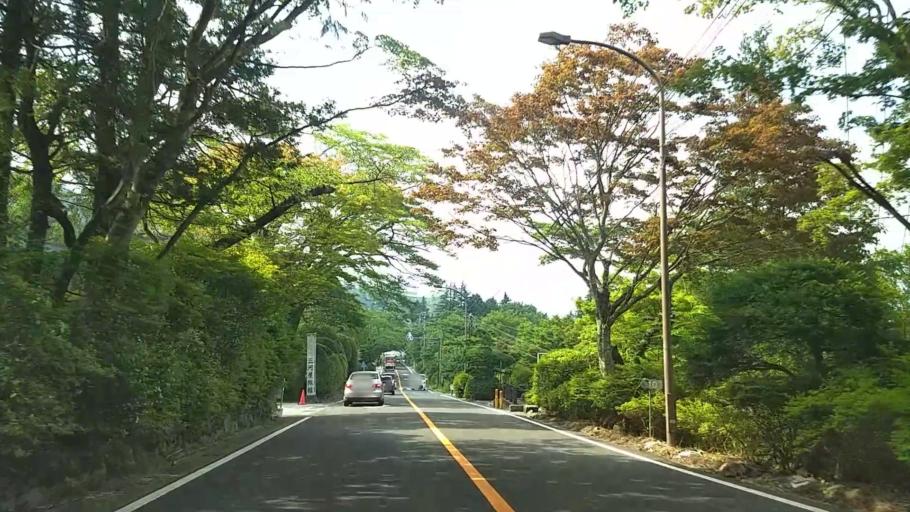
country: JP
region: Kanagawa
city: Hakone
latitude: 35.2363
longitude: 139.0476
